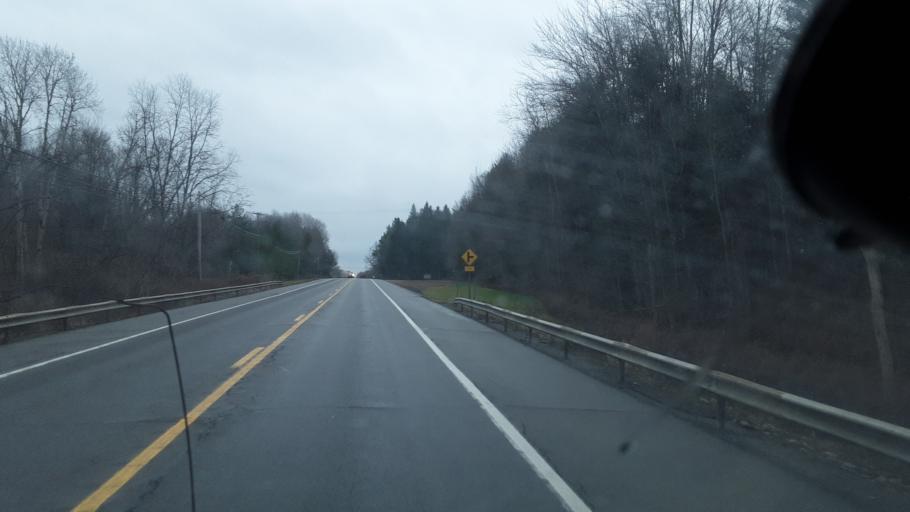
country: US
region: New York
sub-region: Erie County
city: Holland
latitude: 42.6156
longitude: -78.5101
